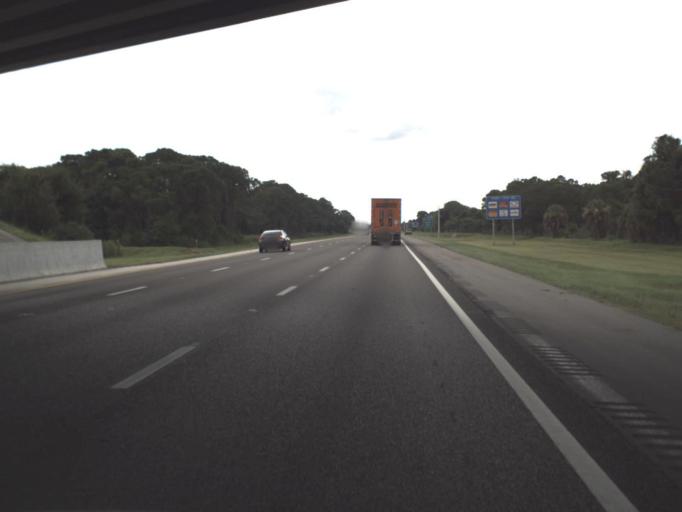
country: US
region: Florida
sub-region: Sarasota County
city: Nokomis
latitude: 27.1229
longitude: -82.3976
